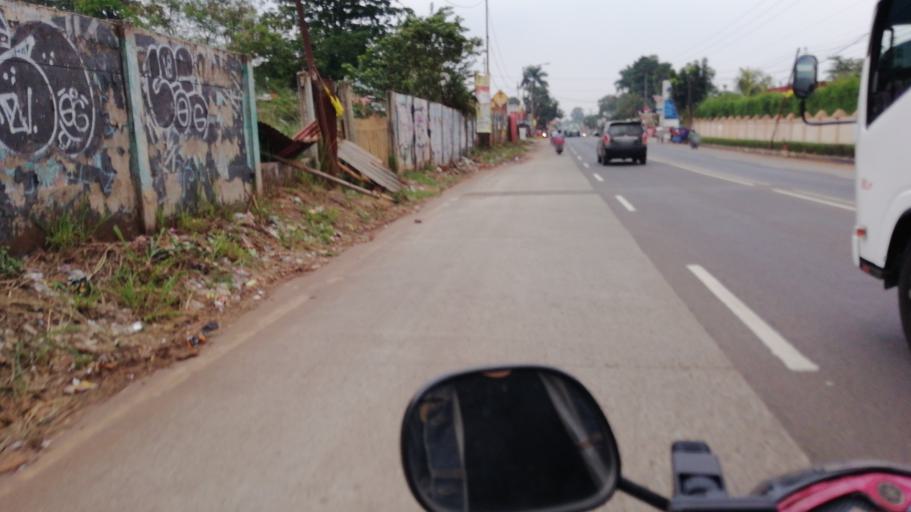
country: ID
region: West Java
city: Parung
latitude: -6.4544
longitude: 106.7311
